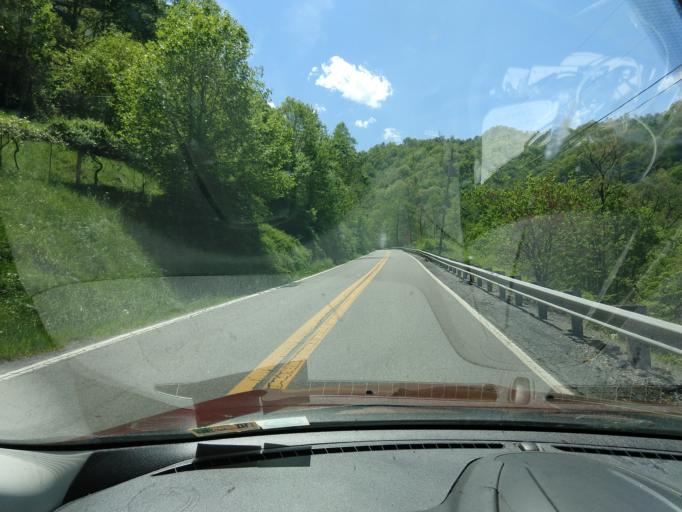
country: US
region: West Virginia
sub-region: McDowell County
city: Welch
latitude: 37.3163
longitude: -81.6955
